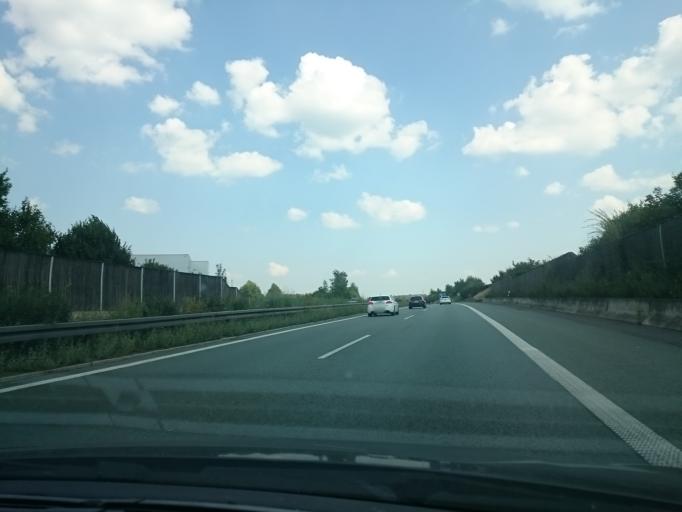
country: DE
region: Saxony
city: Limbach
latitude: 50.5404
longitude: 12.2591
